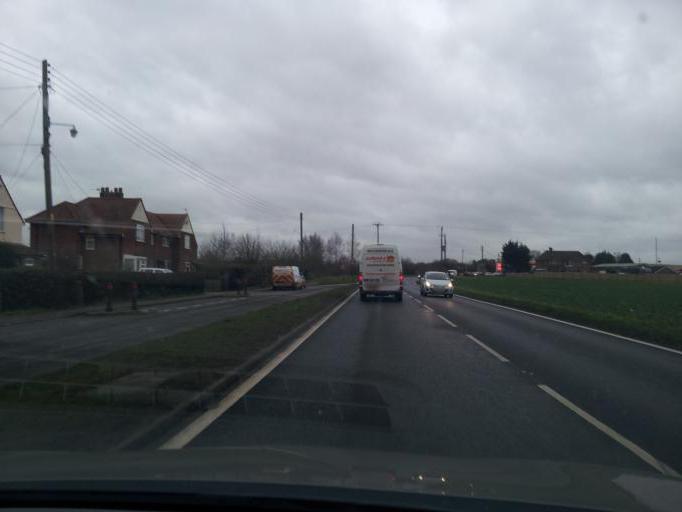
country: GB
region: England
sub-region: Suffolk
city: Ixworth
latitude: 52.3242
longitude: 0.8763
